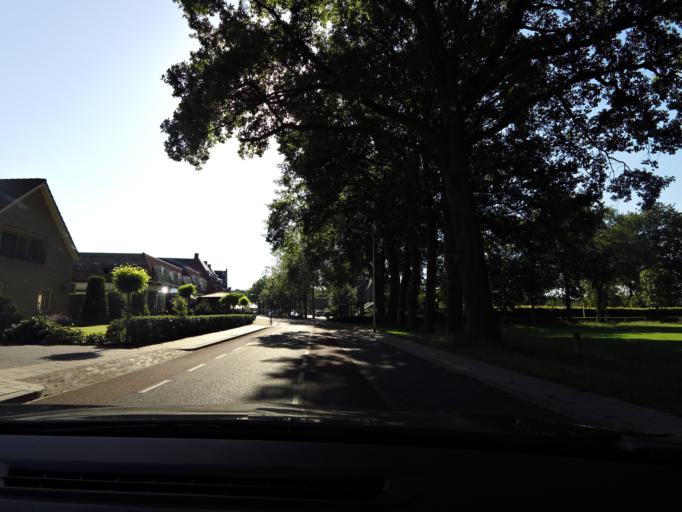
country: NL
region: Overijssel
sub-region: Gemeente Raalte
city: Raalte
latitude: 52.3595
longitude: 6.3811
